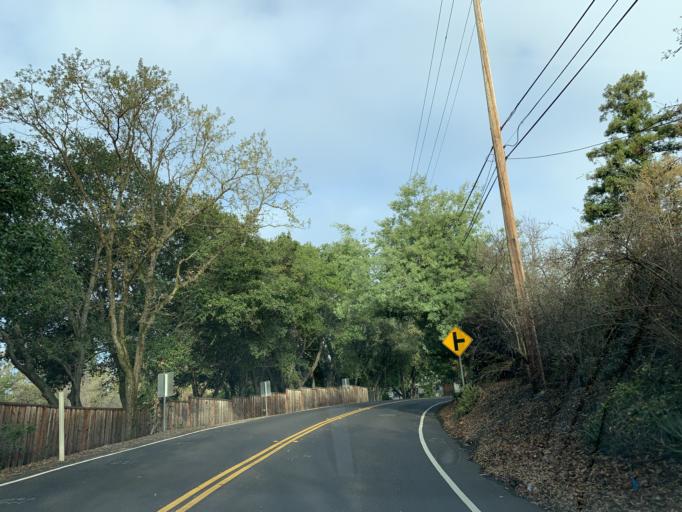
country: US
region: California
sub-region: Contra Costa County
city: Saranap
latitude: 37.8882
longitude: -122.0797
